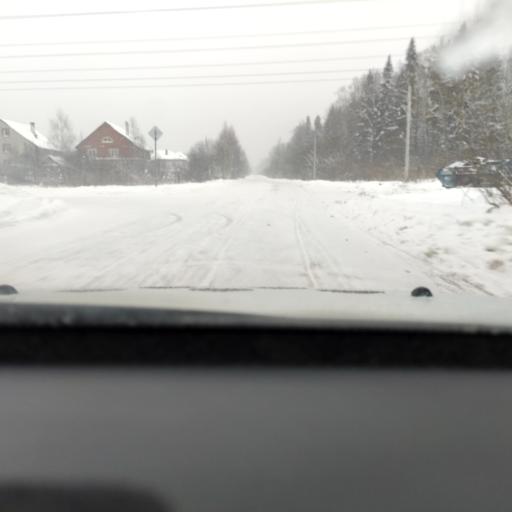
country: RU
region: Perm
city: Polazna
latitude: 58.1452
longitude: 56.4327
